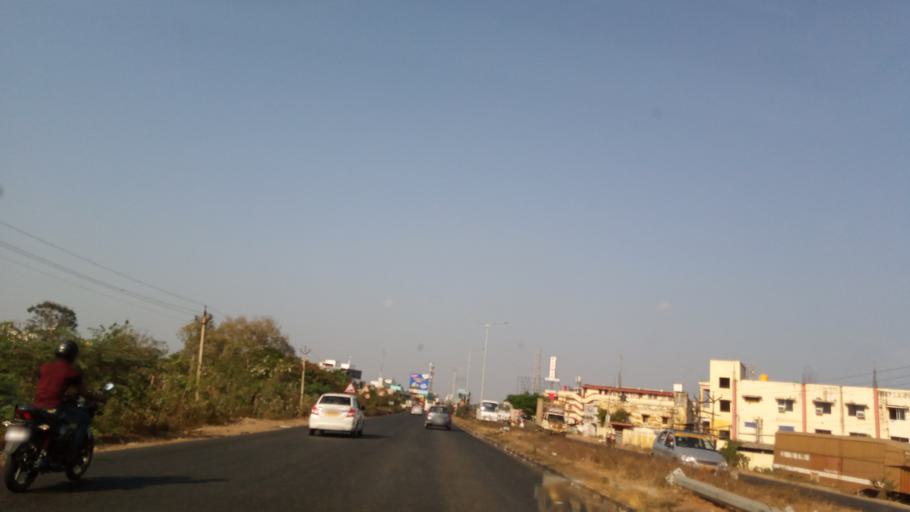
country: IN
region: Tamil Nadu
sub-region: Kancheepuram
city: Nandambakkam
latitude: 13.0140
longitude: 80.0022
